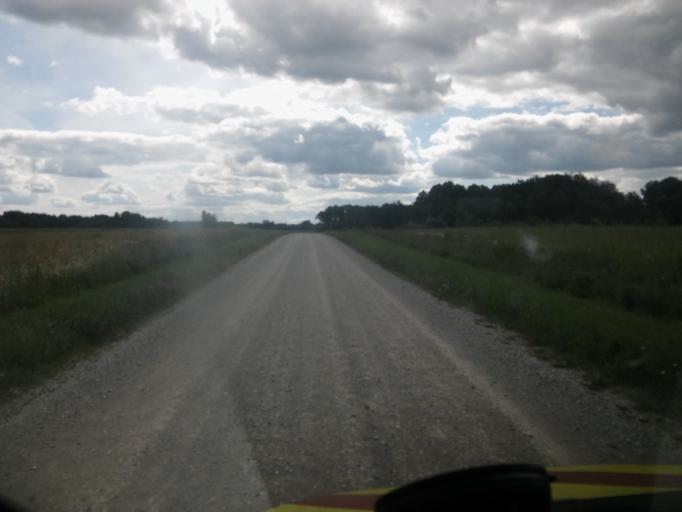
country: EE
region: Viljandimaa
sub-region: Karksi vald
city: Karksi-Nuia
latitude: 58.0965
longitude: 25.4957
